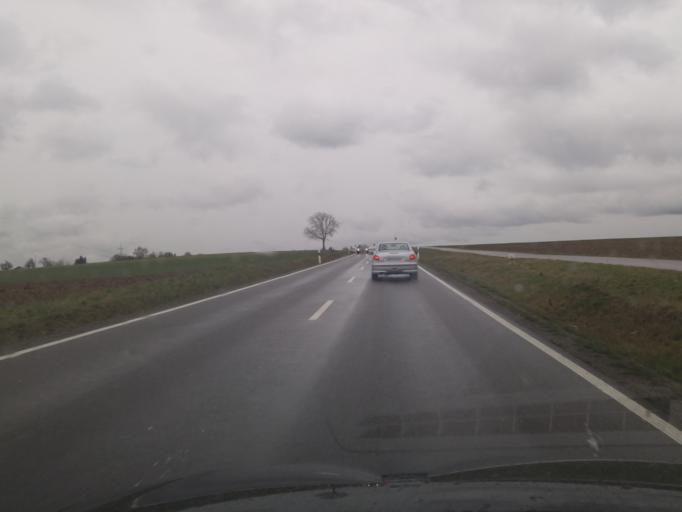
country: DE
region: Baden-Wuerttemberg
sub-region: Regierungsbezirk Stuttgart
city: Schwaikheim
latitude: 48.8905
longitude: 9.3674
